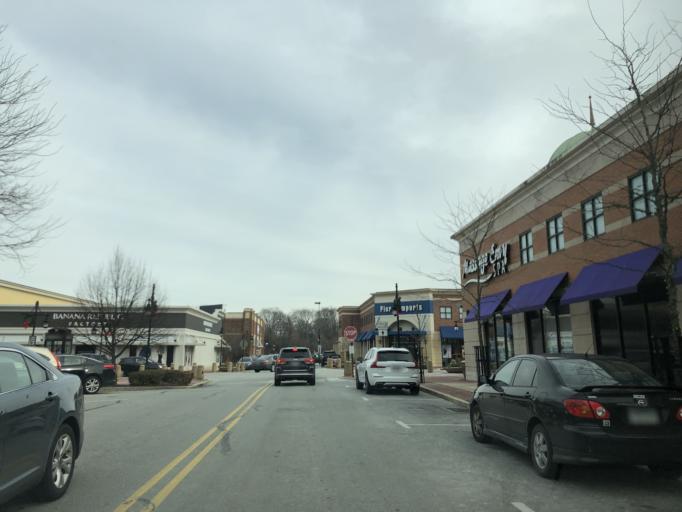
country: US
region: Pennsylvania
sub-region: Chester County
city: Exton
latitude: 40.0232
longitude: -75.6289
